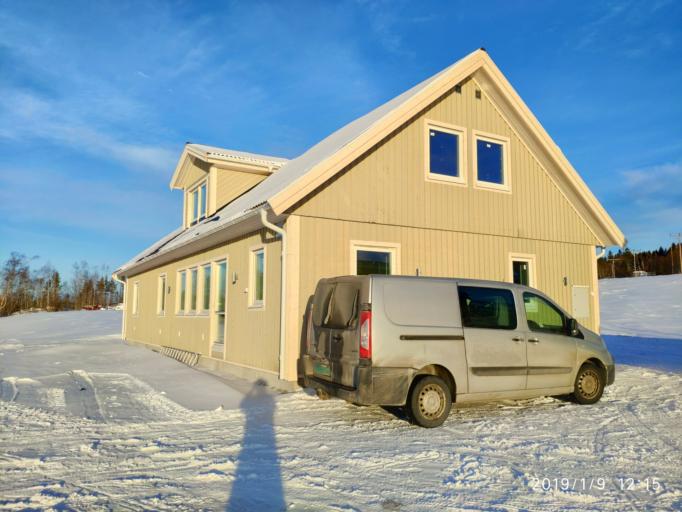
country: NO
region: Hedmark
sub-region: Ringsaker
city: Brumunddal
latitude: 60.9312
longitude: 11.0341
